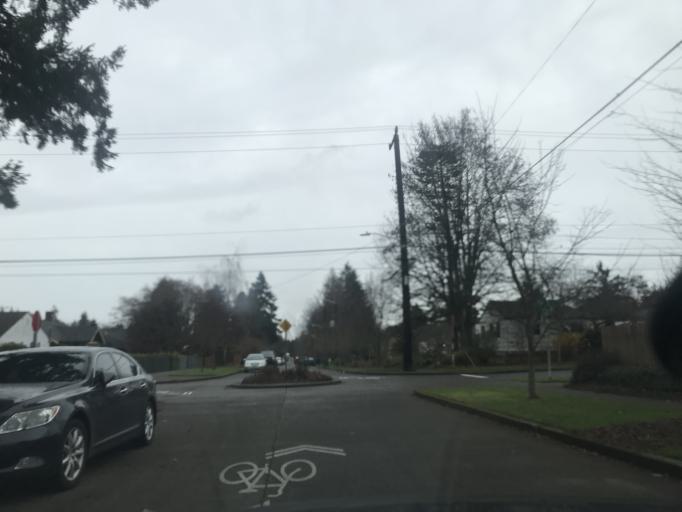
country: US
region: Washington
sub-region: King County
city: White Center
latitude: 47.5280
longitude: -122.3564
